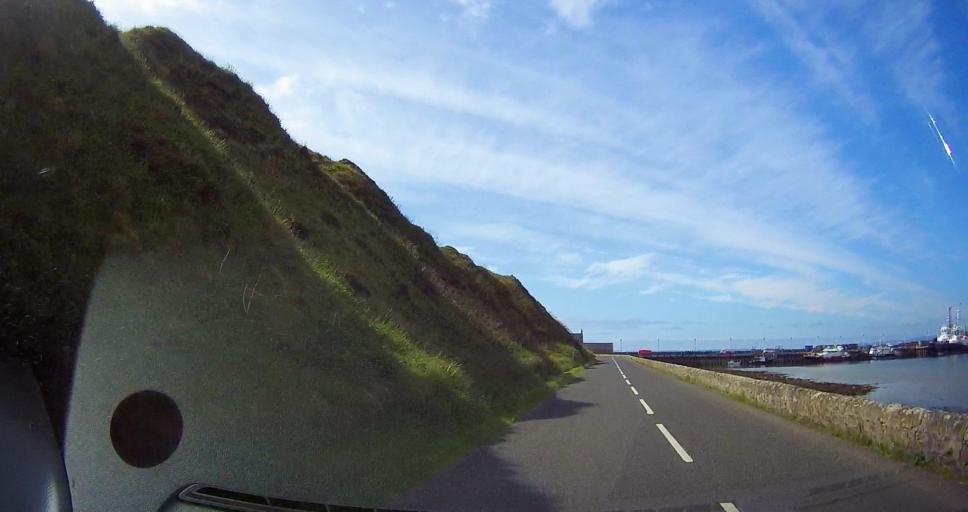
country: GB
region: Scotland
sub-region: Orkney Islands
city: Orkney
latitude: 58.9584
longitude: -2.9689
